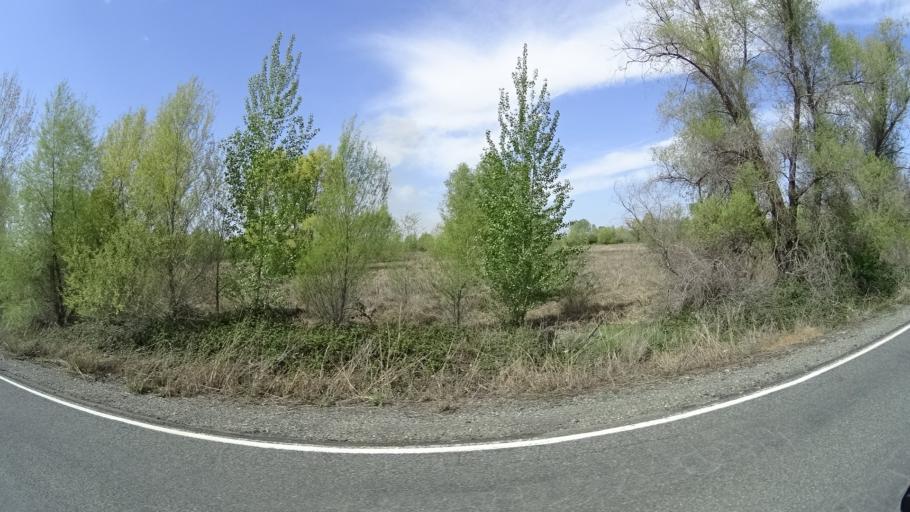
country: US
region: California
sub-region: Butte County
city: Durham
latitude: 39.5228
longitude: -121.8568
